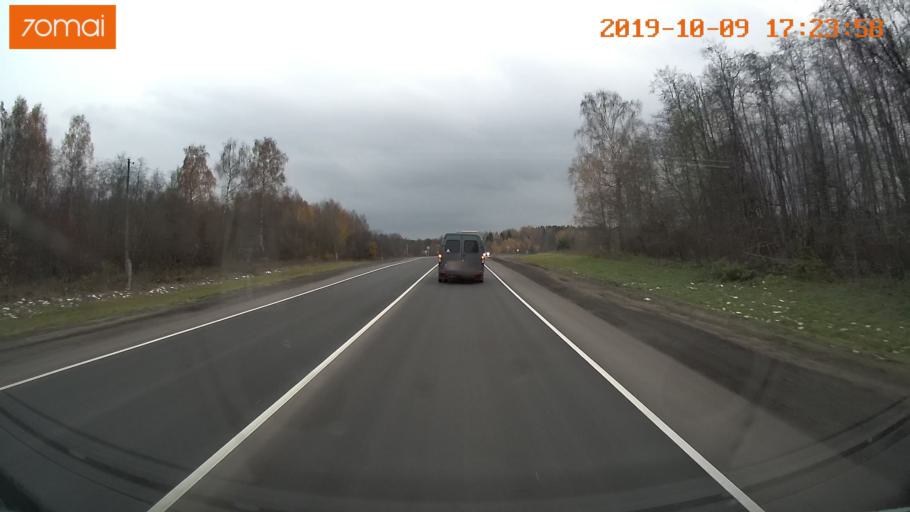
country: RU
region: Ivanovo
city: Furmanov
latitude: 57.1895
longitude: 41.1124
